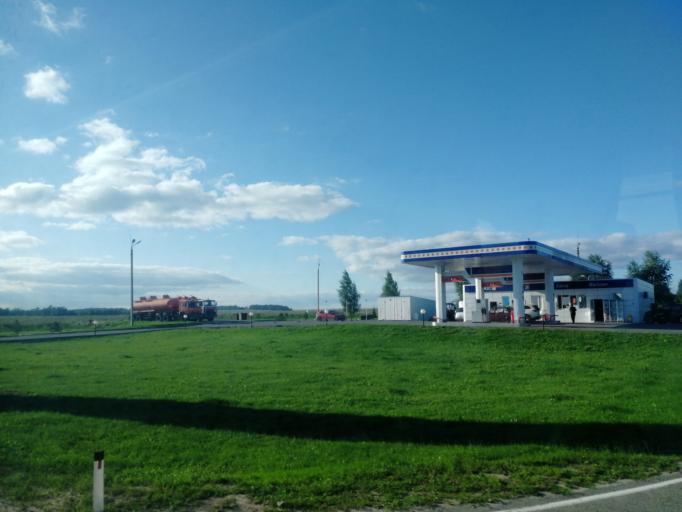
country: RU
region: Tula
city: Dubna
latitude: 54.2826
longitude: 37.1611
